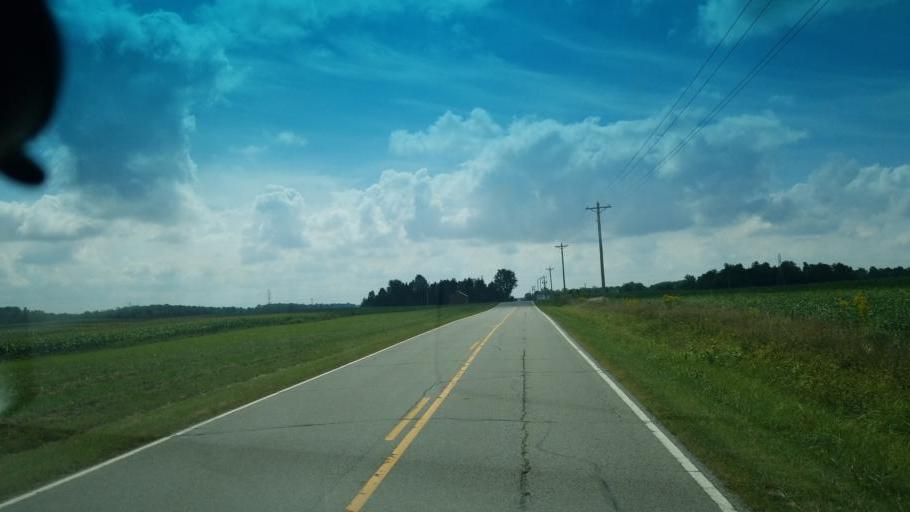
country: US
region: Ohio
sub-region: Crawford County
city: Bucyrus
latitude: 40.9543
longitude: -82.9017
